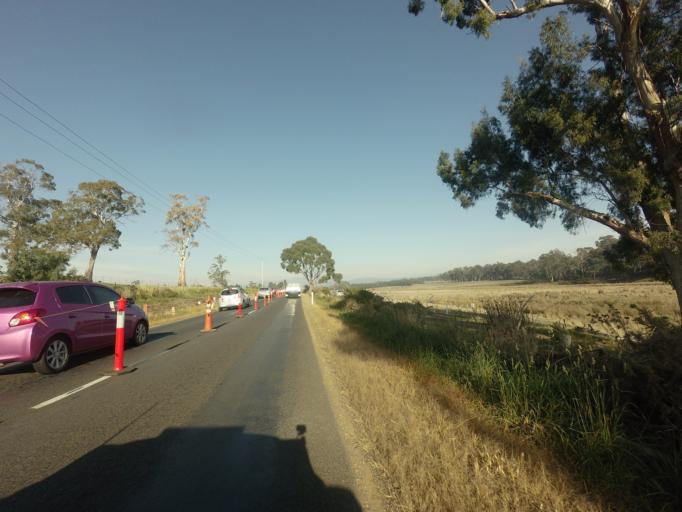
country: AU
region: Tasmania
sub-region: Northern Midlands
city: Longford
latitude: -41.5586
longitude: 146.9854
